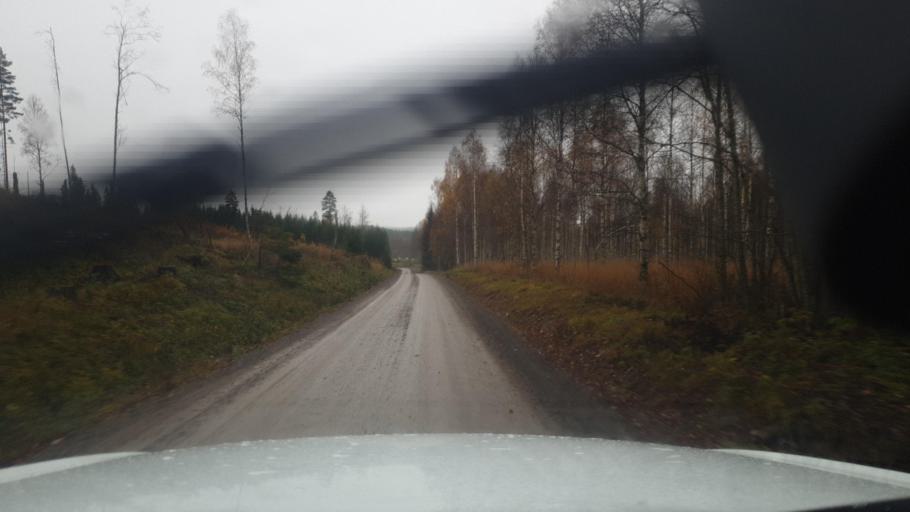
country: SE
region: Vaermland
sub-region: Arvika Kommun
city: Arvika
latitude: 59.9442
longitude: 12.6613
